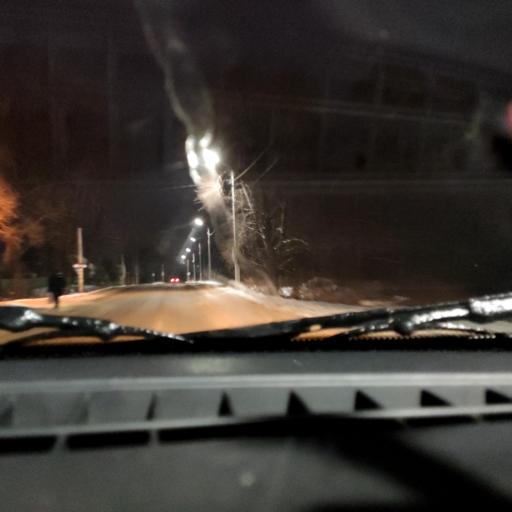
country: RU
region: Bashkortostan
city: Ufa
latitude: 54.6623
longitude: 56.0704
